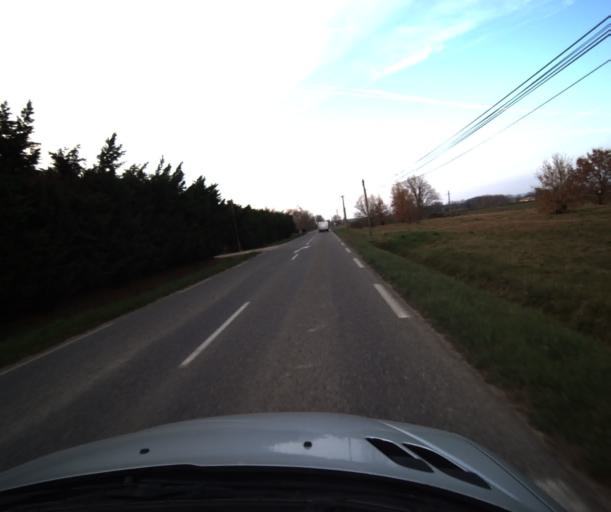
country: FR
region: Midi-Pyrenees
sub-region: Departement de la Haute-Garonne
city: Fronton
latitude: 43.8617
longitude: 1.3831
